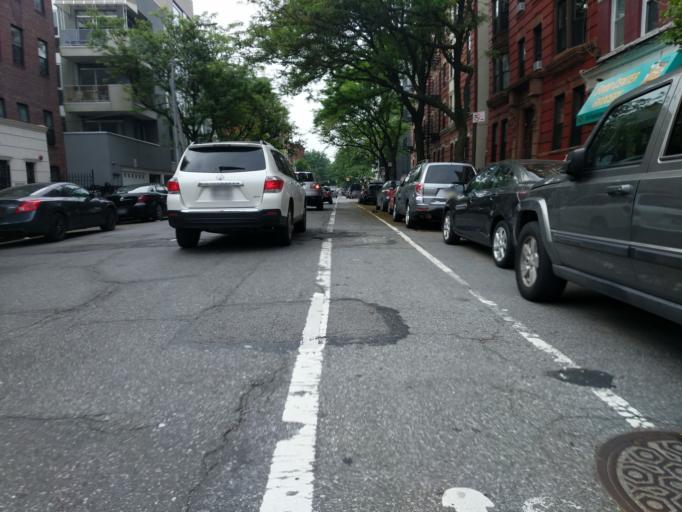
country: US
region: New York
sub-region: Kings County
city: Brooklyn
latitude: 40.6870
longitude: -73.9569
